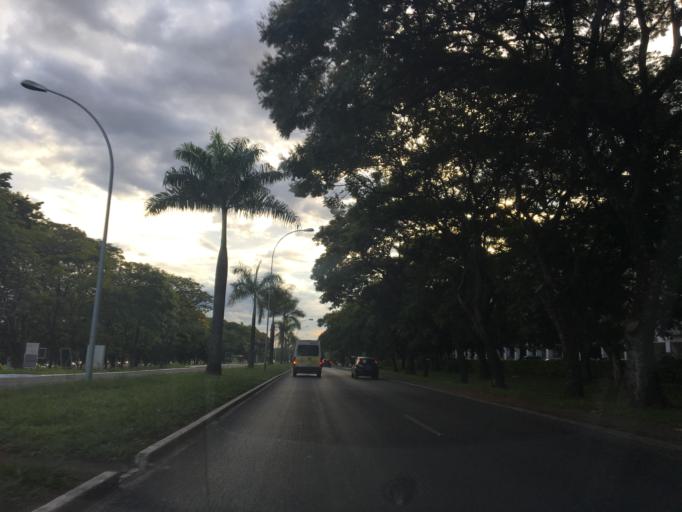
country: BR
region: Federal District
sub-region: Brasilia
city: Brasilia
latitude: -15.8192
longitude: -47.9049
